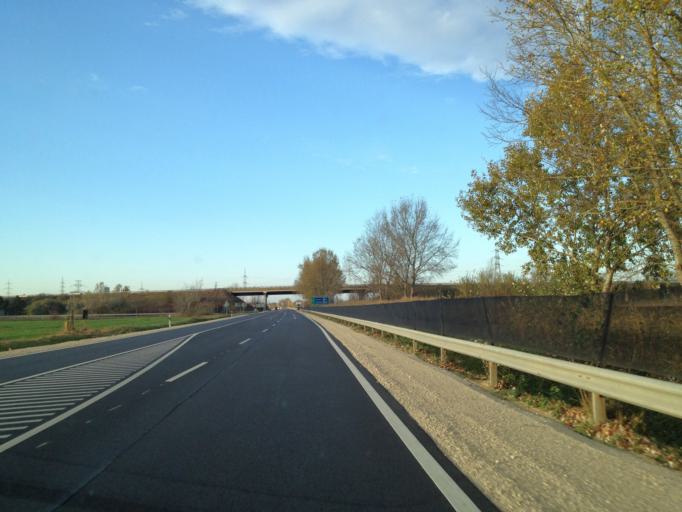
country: HU
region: Gyor-Moson-Sopron
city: Gyorujbarat
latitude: 47.6301
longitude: 17.6719
